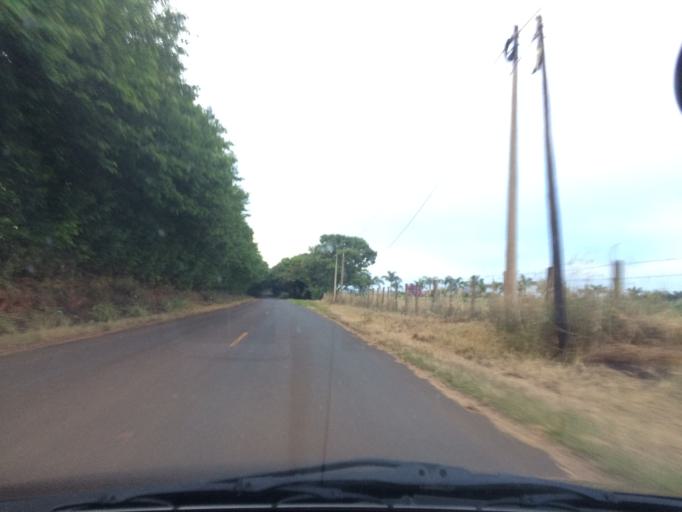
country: BR
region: Sao Paulo
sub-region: Casa Branca
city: Casa Branca
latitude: -21.7354
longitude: -47.1780
